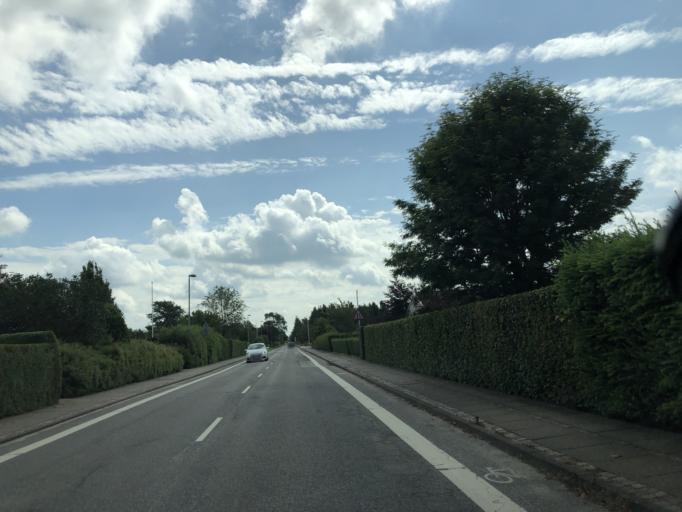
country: DK
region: Central Jutland
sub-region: Ikast-Brande Kommune
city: Brande
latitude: 55.9397
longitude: 9.1475
